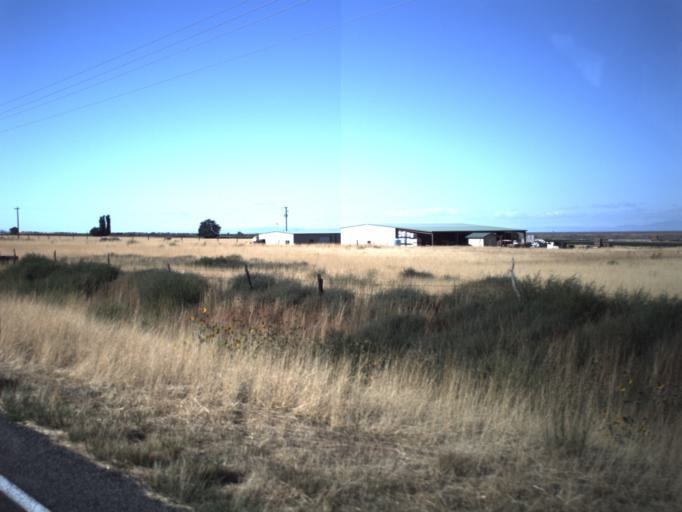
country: US
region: Utah
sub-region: Millard County
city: Delta
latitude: 39.4161
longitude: -112.3297
